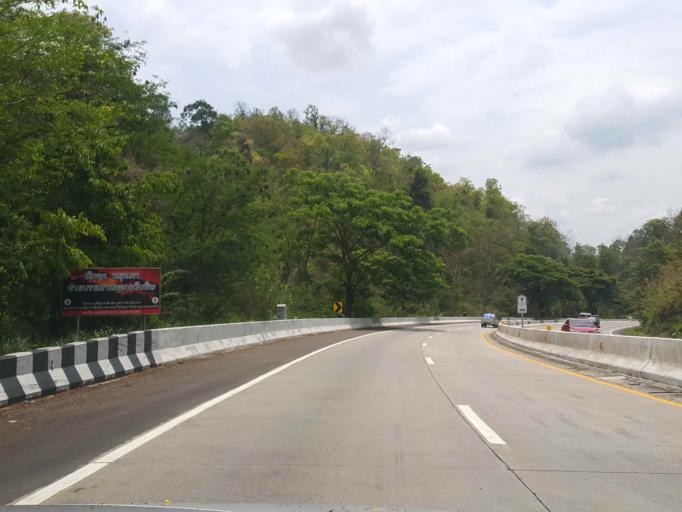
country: TH
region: Lamphun
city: Mae Tha
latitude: 18.4060
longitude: 99.2122
